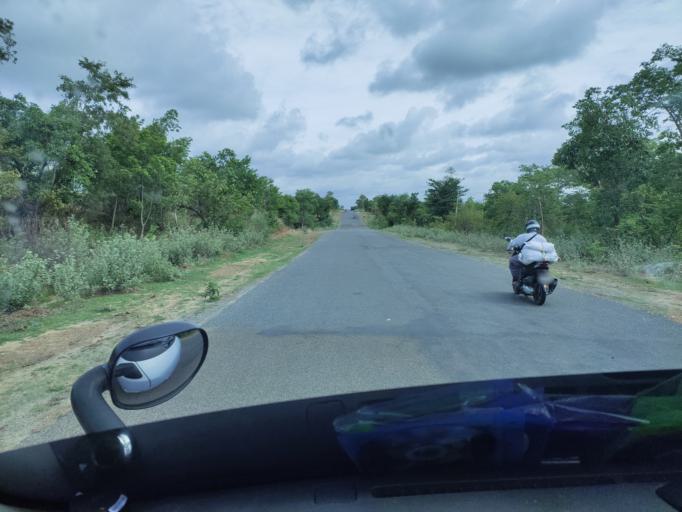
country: MM
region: Magway
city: Chauk
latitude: 20.9728
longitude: 95.0543
